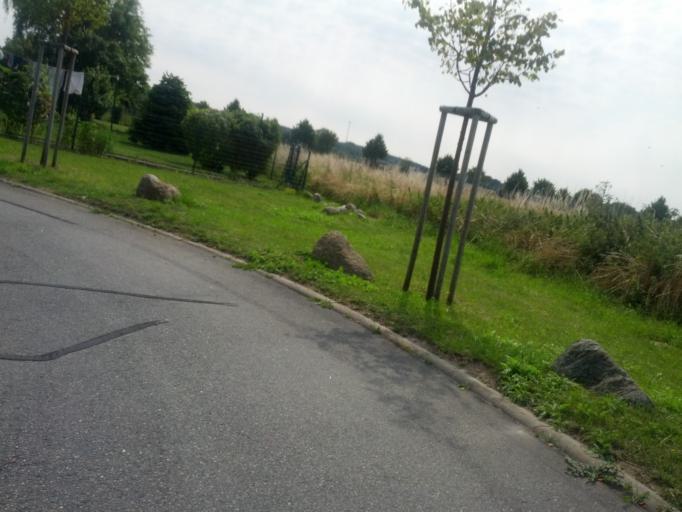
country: DE
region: Mecklenburg-Vorpommern
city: Bastorf
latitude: 54.1409
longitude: 11.7210
